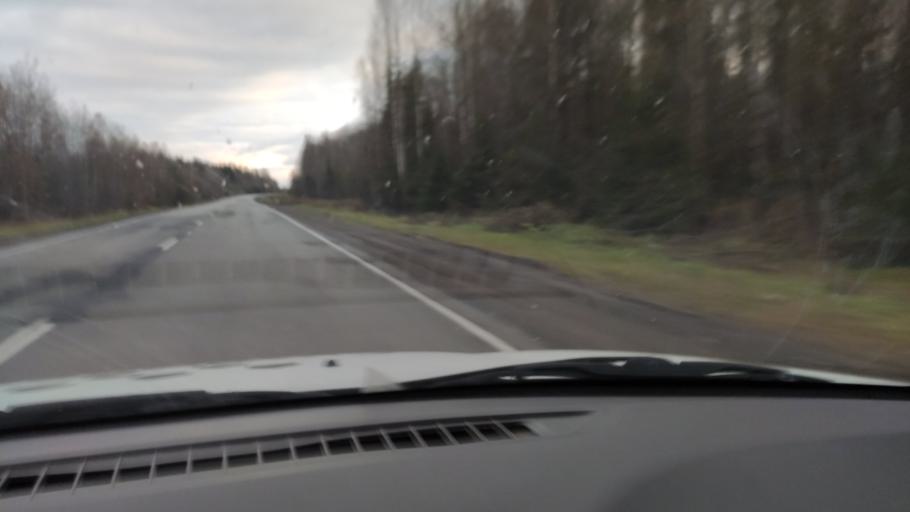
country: RU
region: Kirov
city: Omutninsk
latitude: 58.7549
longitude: 52.0414
